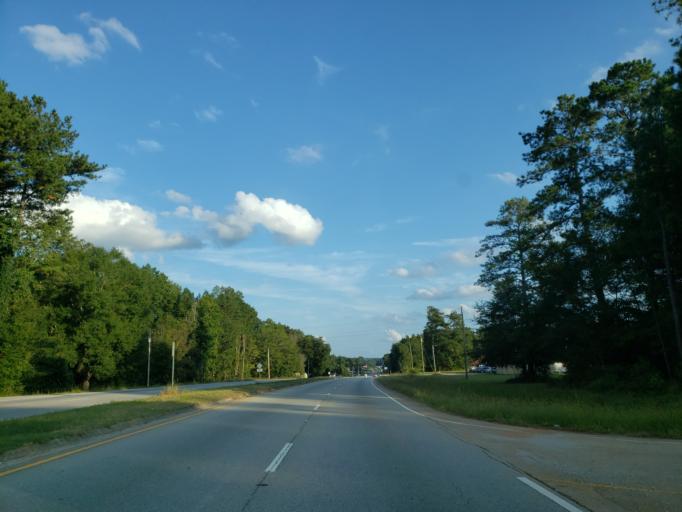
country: US
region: Georgia
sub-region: Carroll County
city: Carrollton
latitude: 33.6229
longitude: -85.0999
